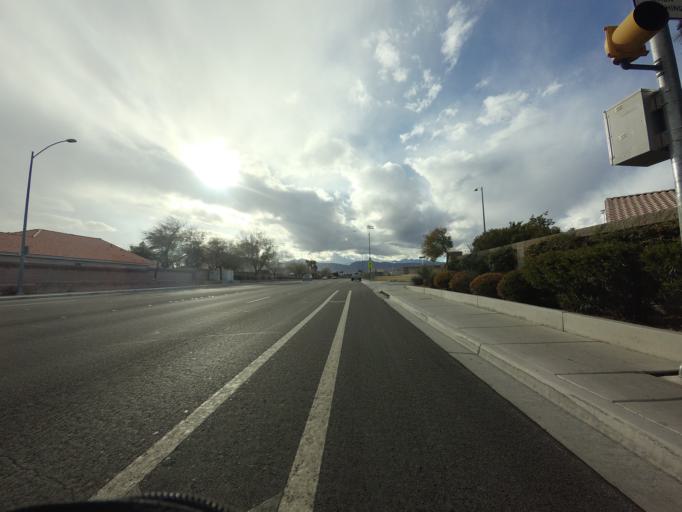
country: US
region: Nevada
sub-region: Clark County
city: North Las Vegas
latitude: 36.2688
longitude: -115.2112
